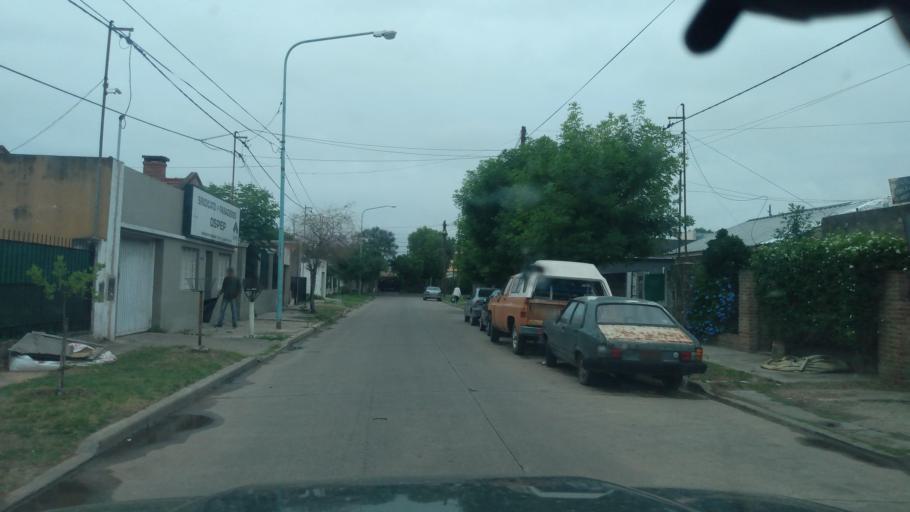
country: AR
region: Buenos Aires
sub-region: Partido de Lujan
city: Lujan
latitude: -34.5760
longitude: -59.1192
